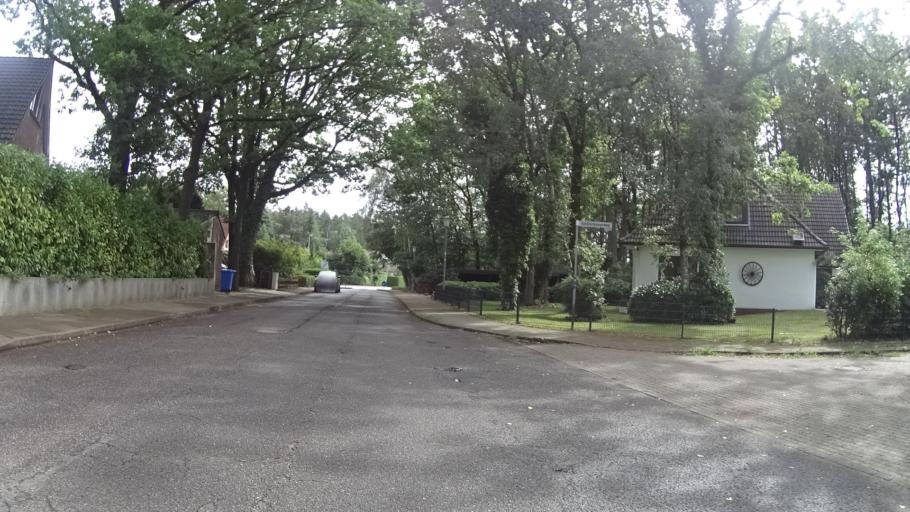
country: DE
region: Schleswig-Holstein
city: Henstedt-Ulzburg
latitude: 53.7615
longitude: 9.9959
